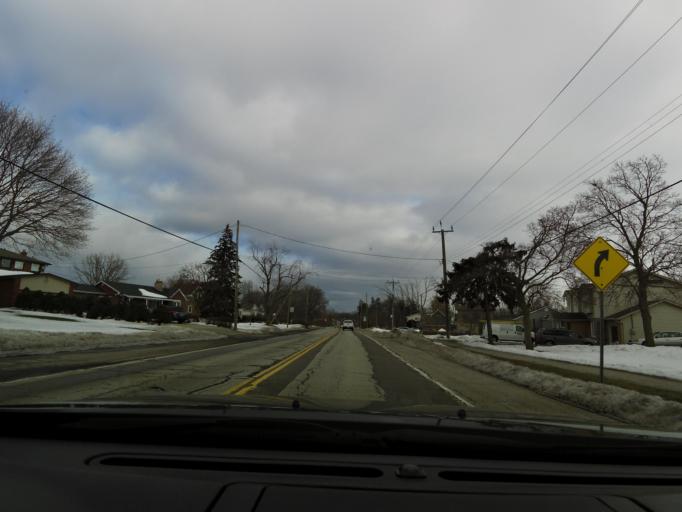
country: CA
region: Ontario
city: Hamilton
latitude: 43.2071
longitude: -79.6434
